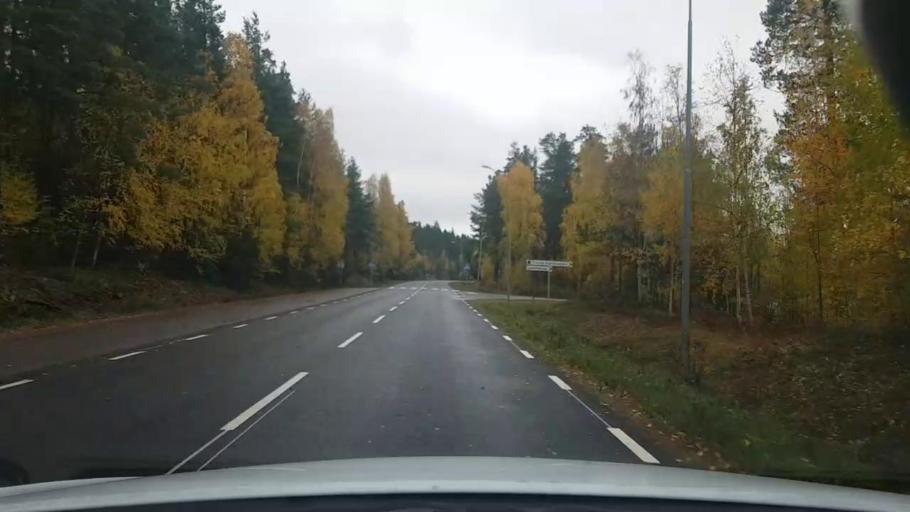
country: SE
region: OErebro
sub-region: Laxa Kommun
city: Laxa
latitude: 58.7776
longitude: 14.5362
